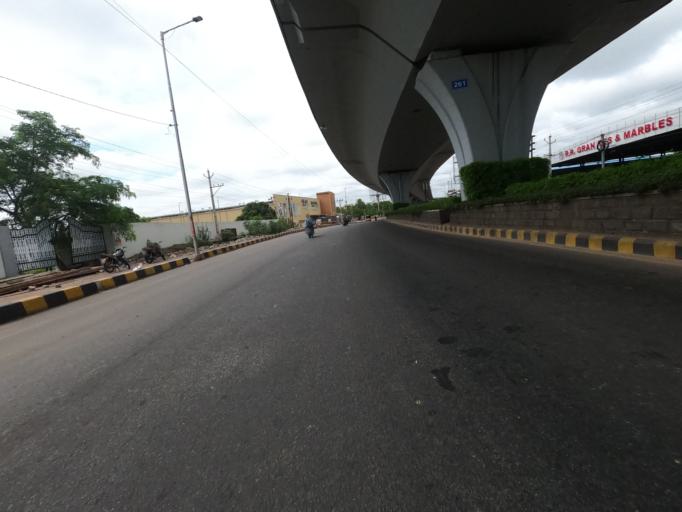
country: IN
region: Telangana
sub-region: Hyderabad
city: Hyderabad
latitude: 17.3367
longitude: 78.4264
